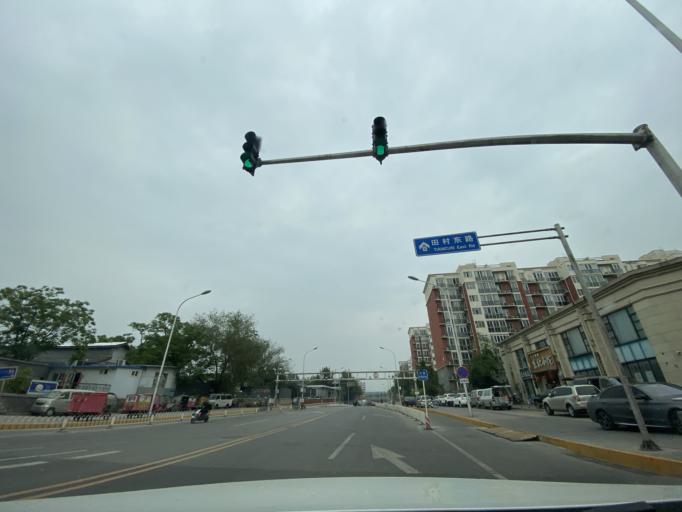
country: CN
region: Beijing
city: Babaoshan
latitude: 39.9285
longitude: 116.2423
